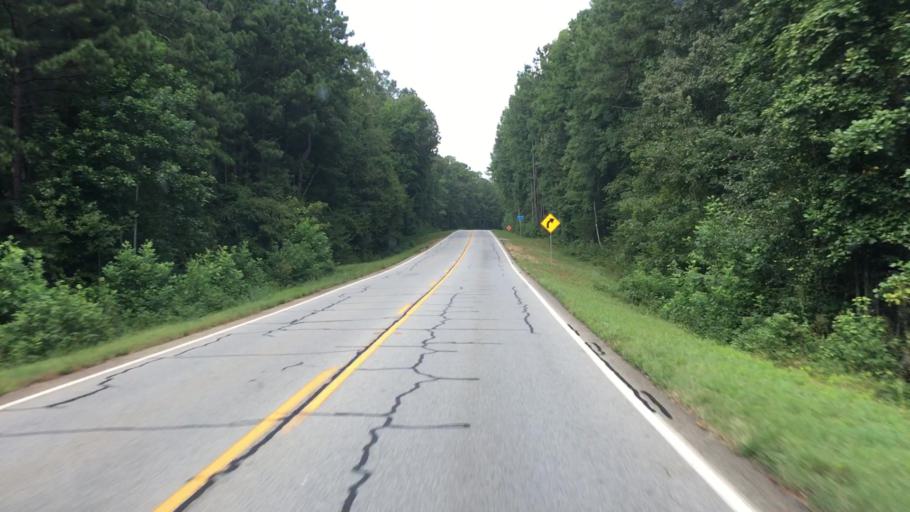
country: US
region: Georgia
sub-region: Butts County
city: Indian Springs
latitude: 33.1682
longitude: -83.8138
